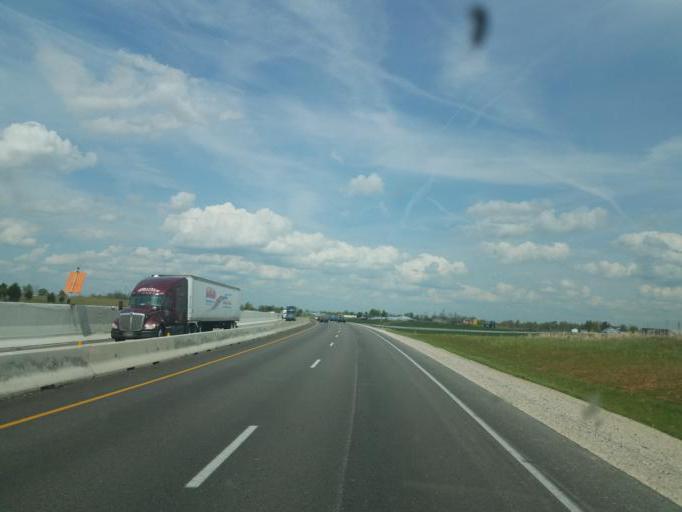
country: US
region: Kentucky
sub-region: Larue County
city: Hodgenville
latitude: 37.4923
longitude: -85.8808
